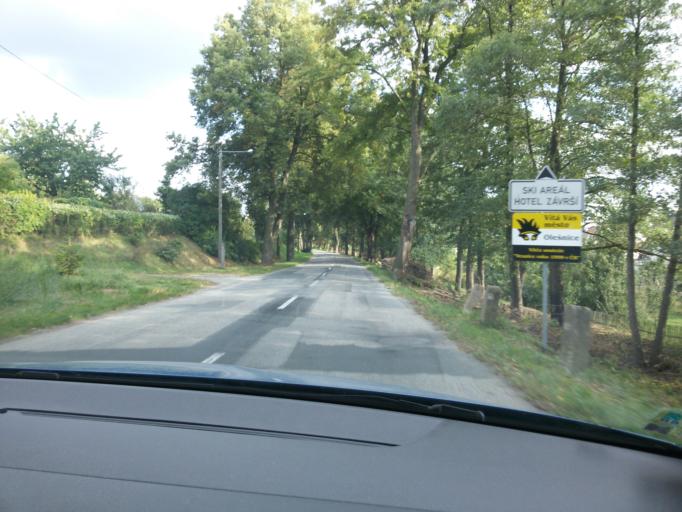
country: CZ
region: South Moravian
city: Olesnice
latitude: 49.5629
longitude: 16.4159
